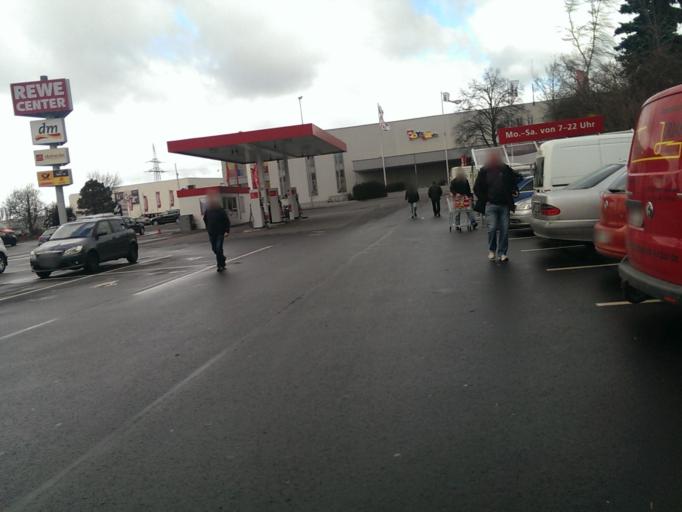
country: DE
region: Lower Saxony
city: Hildesheim
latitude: 52.1638
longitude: 9.9706
